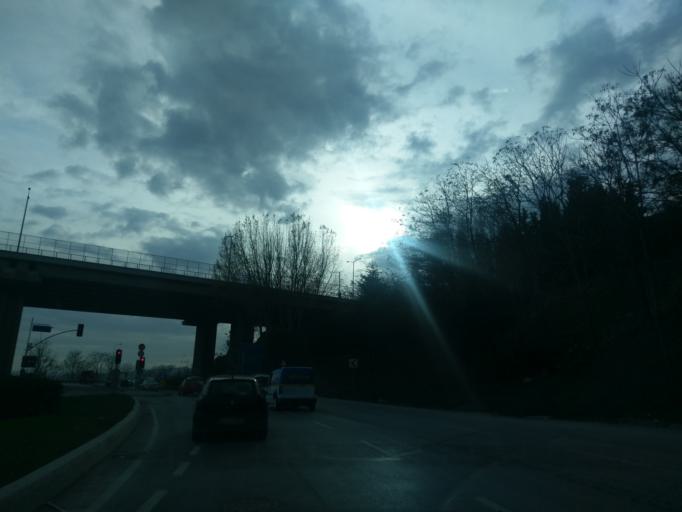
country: TR
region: Istanbul
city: Esenyurt
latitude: 41.0599
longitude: 28.6966
